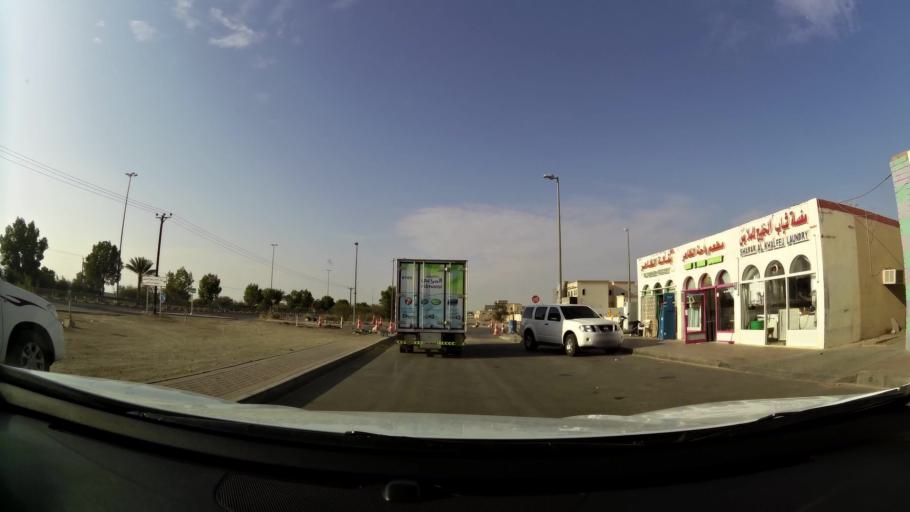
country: AE
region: Abu Dhabi
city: Al Ain
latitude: 24.0792
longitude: 55.8340
